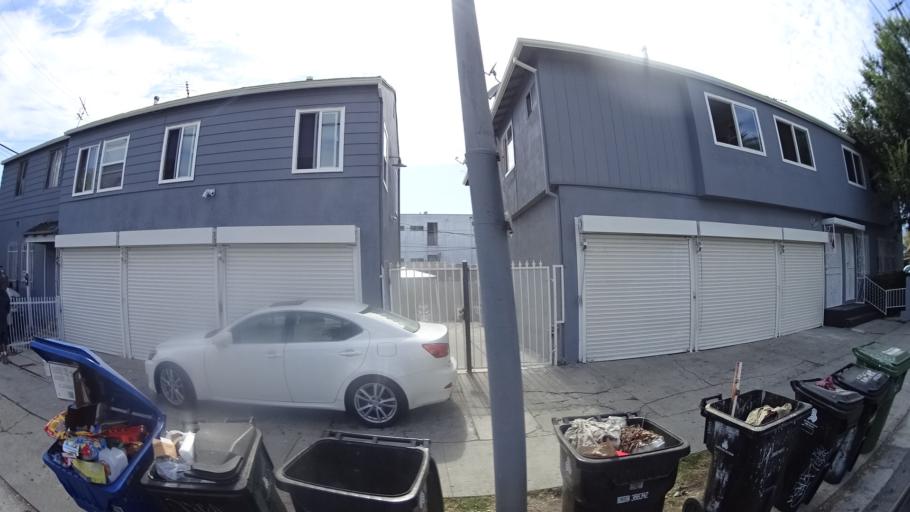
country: US
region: California
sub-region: Los Angeles County
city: Hollywood
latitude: 34.0926
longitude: -118.3136
